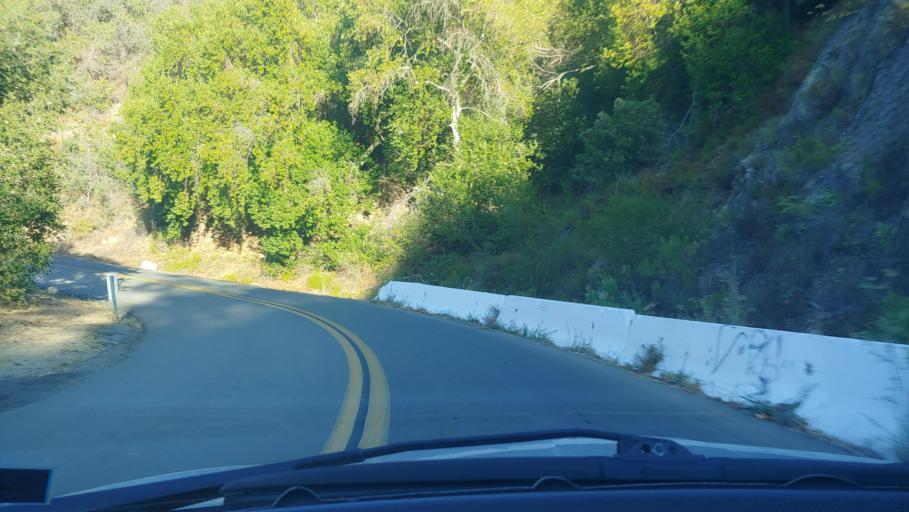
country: US
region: California
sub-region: Santa Barbara County
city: Goleta
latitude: 34.5226
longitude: -119.8359
